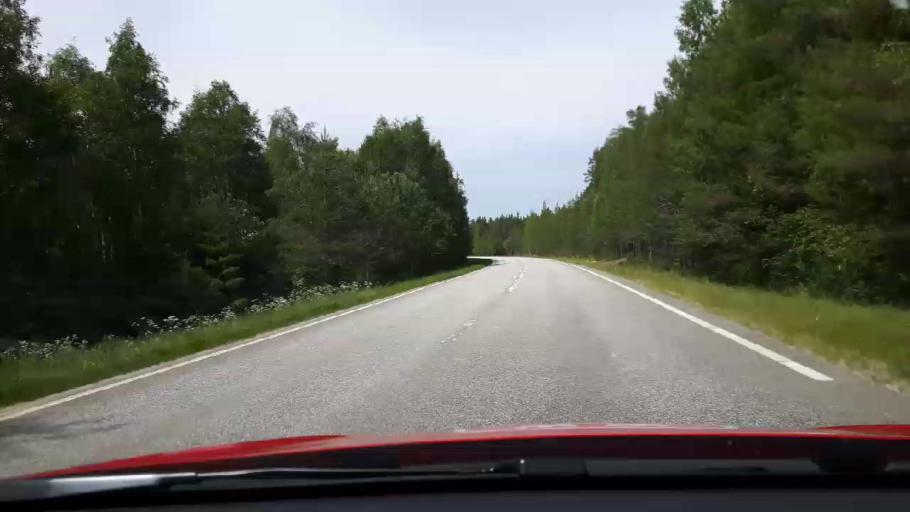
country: SE
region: Jaemtland
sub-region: Harjedalens Kommun
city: Sveg
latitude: 62.1324
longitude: 14.0552
